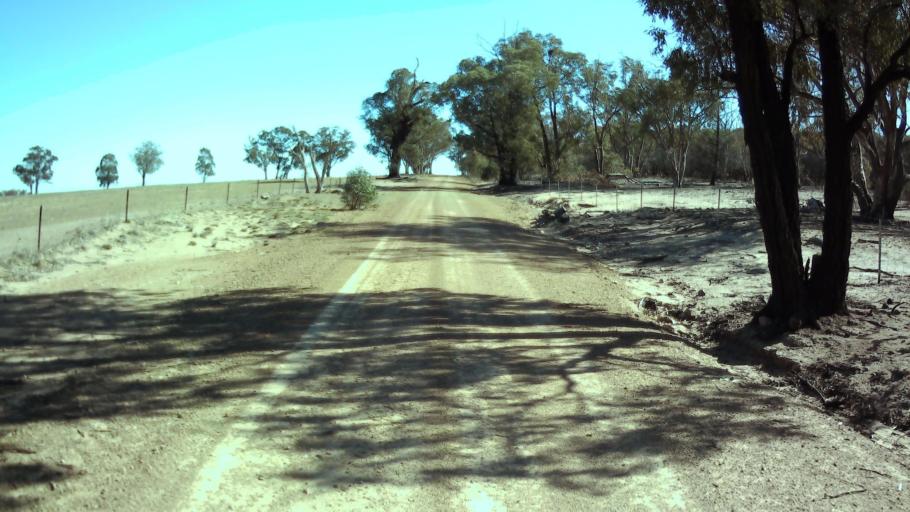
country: AU
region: New South Wales
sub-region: Weddin
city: Grenfell
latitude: -33.7563
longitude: 147.9198
